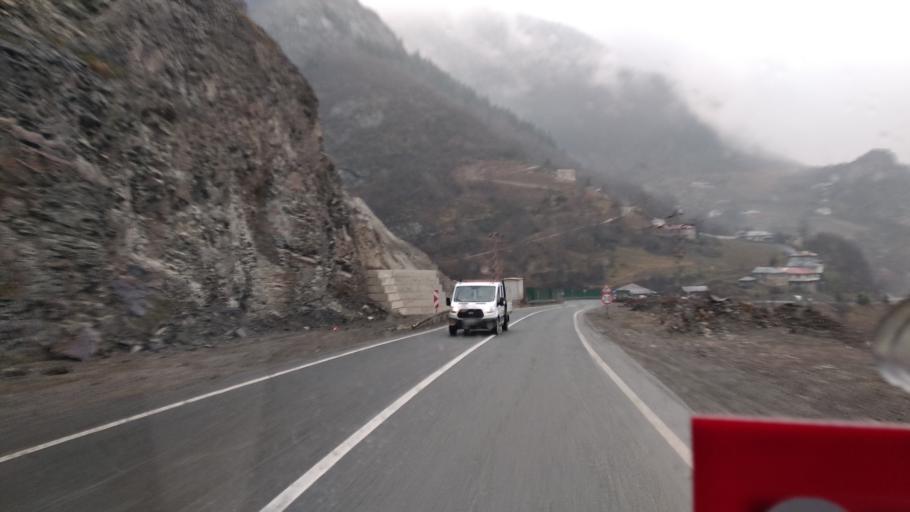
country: TR
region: Trabzon
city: Macka
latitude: 40.7252
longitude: 39.5231
